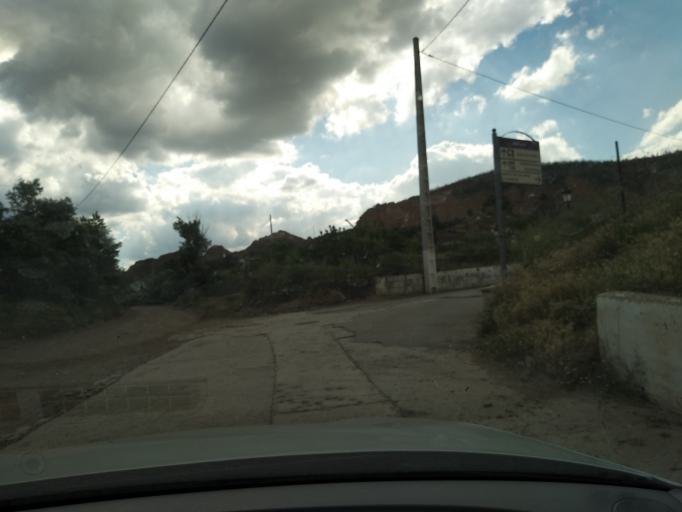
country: ES
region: Andalusia
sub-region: Provincia de Granada
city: Marchal
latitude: 37.2947
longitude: -3.2025
